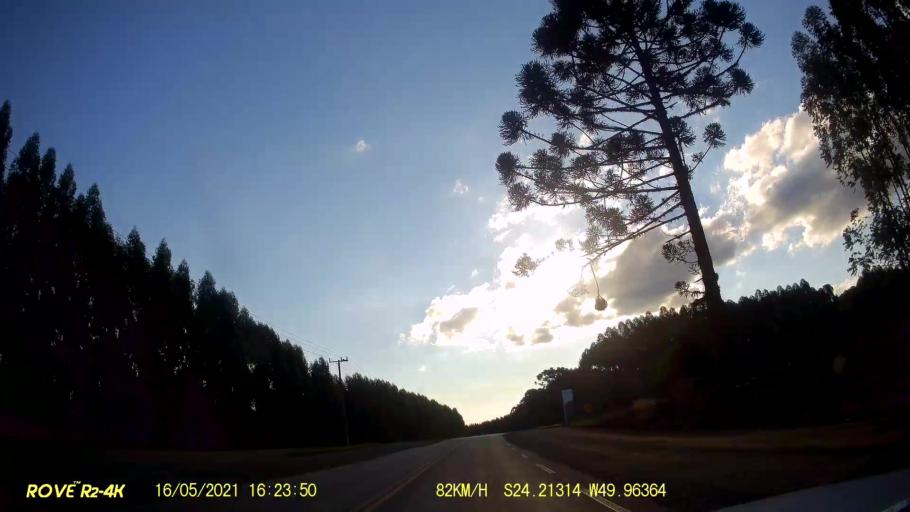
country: BR
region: Parana
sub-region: Jaguariaiva
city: Jaguariaiva
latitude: -24.2131
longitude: -49.9638
